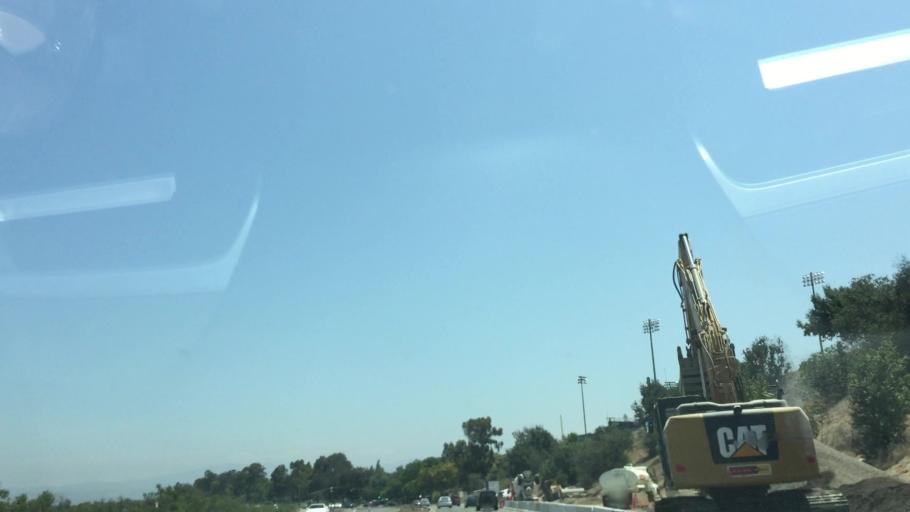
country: US
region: California
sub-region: Orange County
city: Irvine
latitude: 33.6513
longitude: -117.8503
